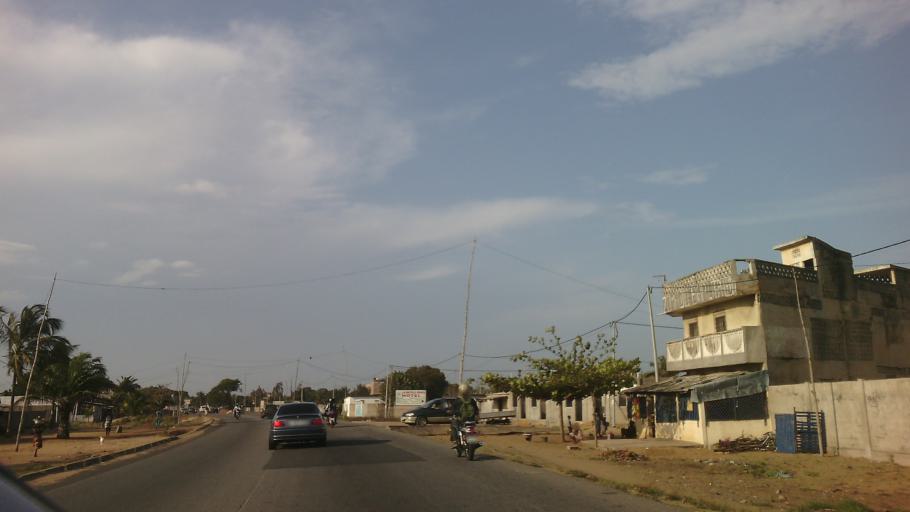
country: TG
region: Maritime
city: Lome
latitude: 6.1840
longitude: 1.3932
